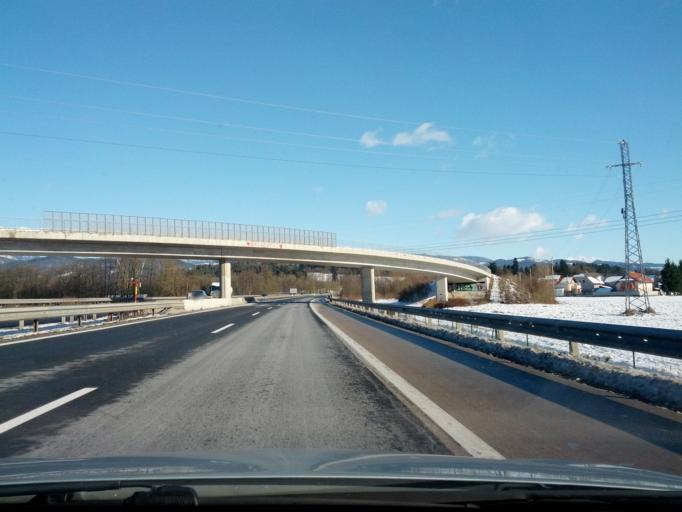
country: SI
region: Domzale
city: Dob
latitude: 46.1481
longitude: 14.6392
